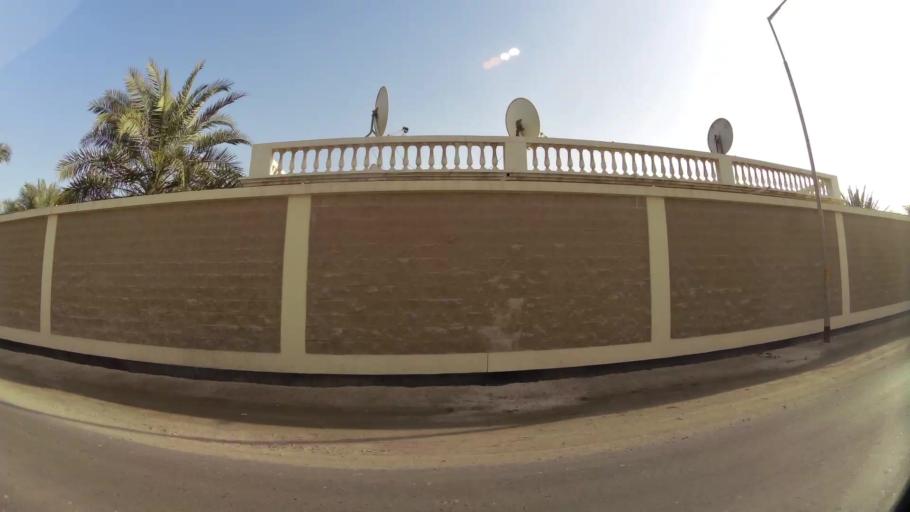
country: BH
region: Manama
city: Jidd Hafs
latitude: 26.2032
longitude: 50.4933
